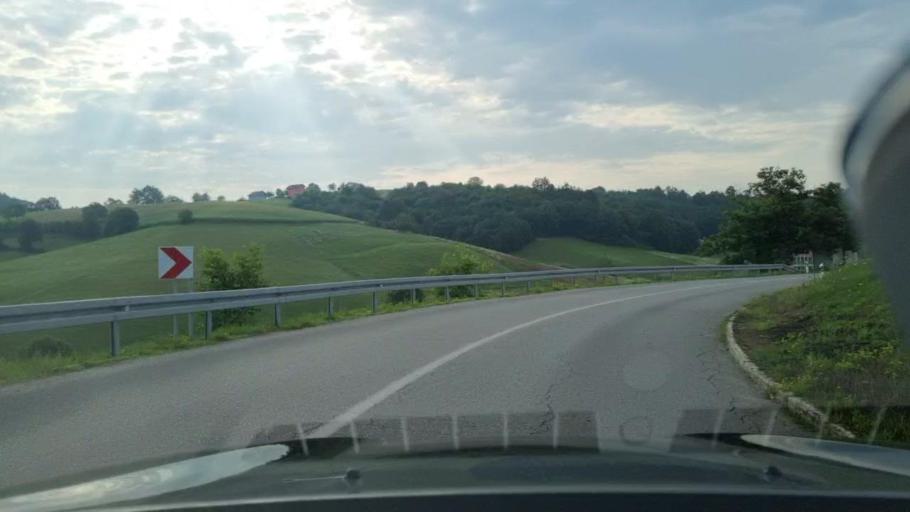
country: BA
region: Federation of Bosnia and Herzegovina
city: Podzvizd
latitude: 45.1780
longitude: 15.8588
